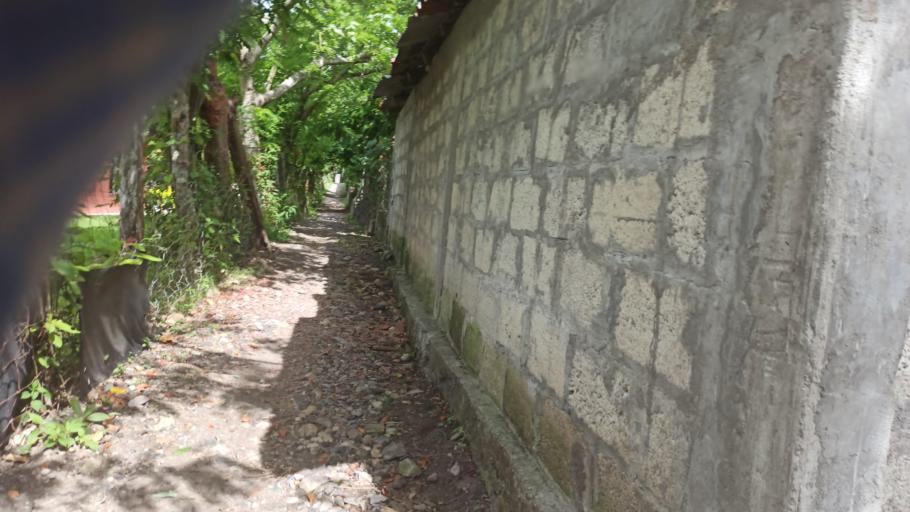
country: MX
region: Veracruz
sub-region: Papantla
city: Residencial Tajin
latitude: 20.6316
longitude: -97.3671
